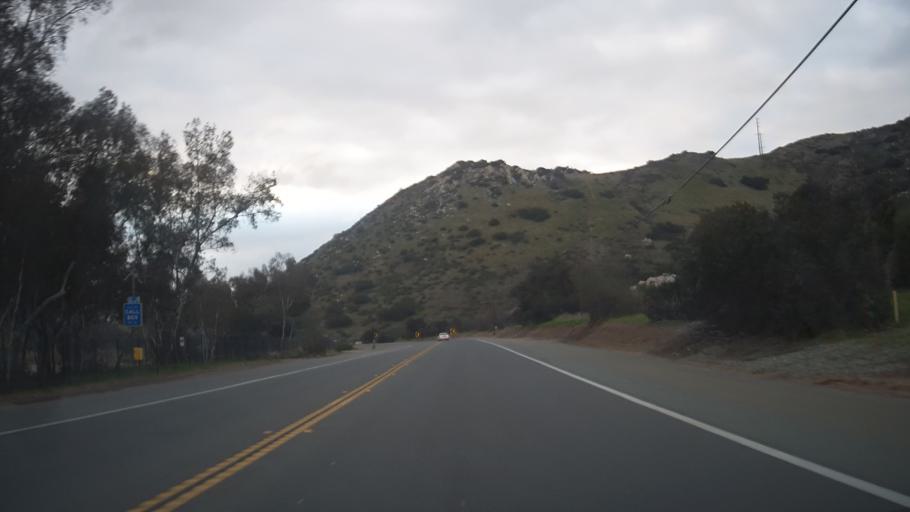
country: US
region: California
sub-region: San Diego County
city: Crest
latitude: 32.7803
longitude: -116.8638
